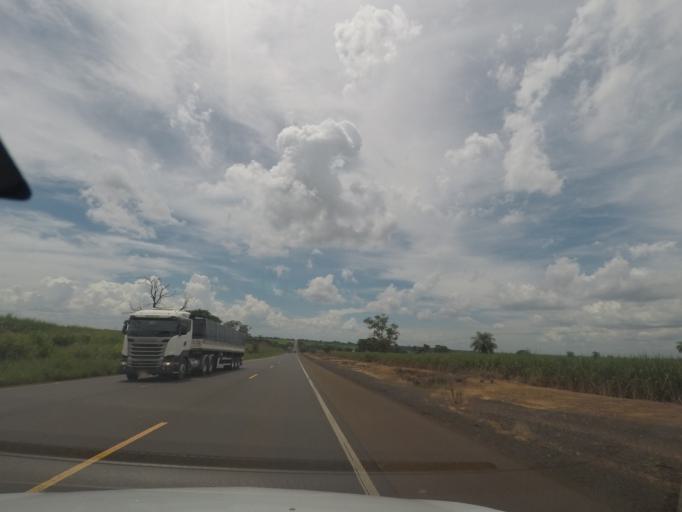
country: BR
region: Sao Paulo
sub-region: Barretos
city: Barretos
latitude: -20.3763
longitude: -48.6439
